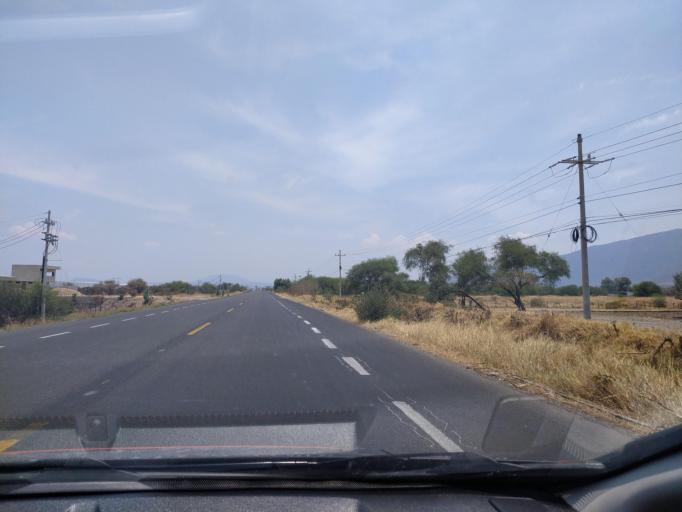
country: MX
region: Jalisco
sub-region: Acatlan de Juarez
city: Villa de los Ninos
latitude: 20.3326
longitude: -103.5907
